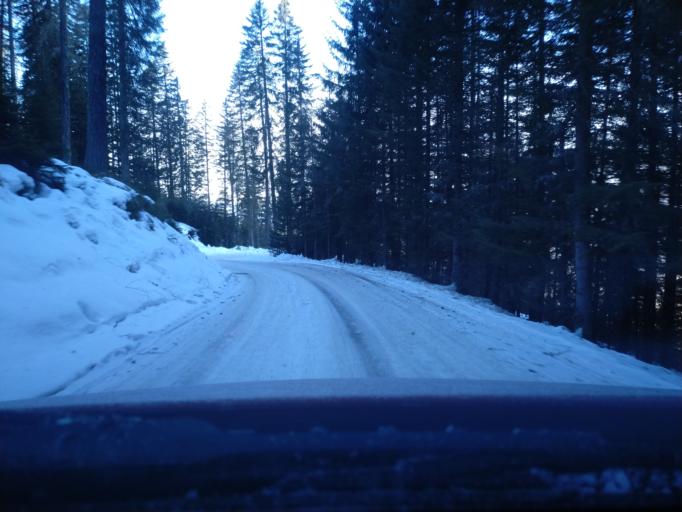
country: AT
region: Carinthia
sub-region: Politischer Bezirk Villach Land
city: Arriach
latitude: 46.7017
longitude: 13.8980
